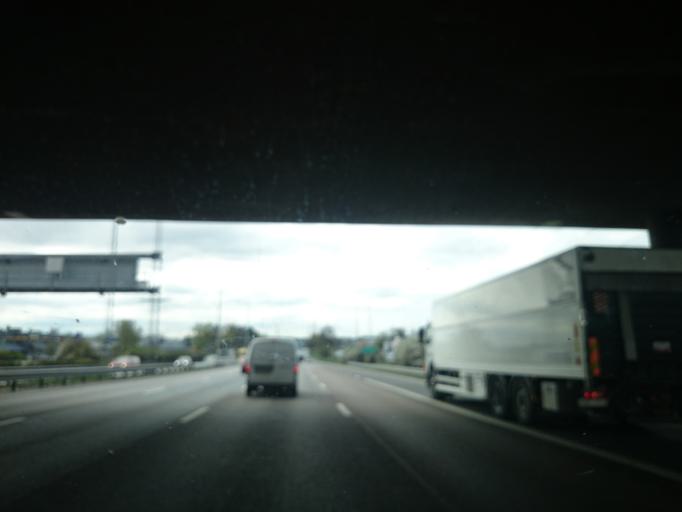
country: SE
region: Stockholm
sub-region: Huddinge Kommun
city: Segeltorp
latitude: 59.2877
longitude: 17.9484
